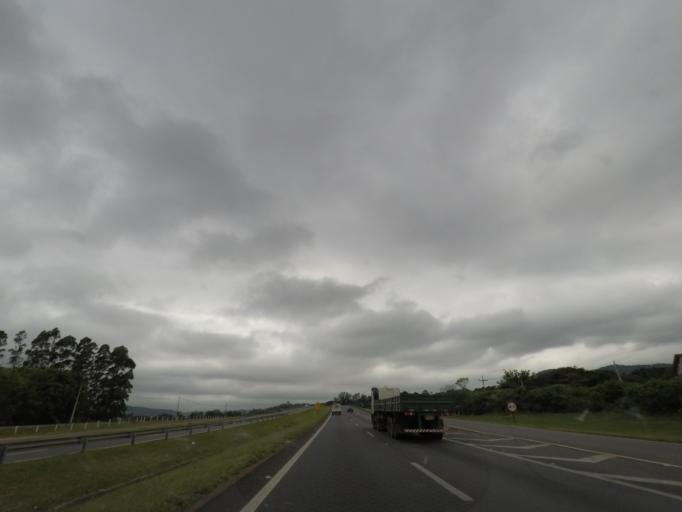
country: BR
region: Sao Paulo
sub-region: Atibaia
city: Atibaia
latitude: -23.1055
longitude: -46.5238
